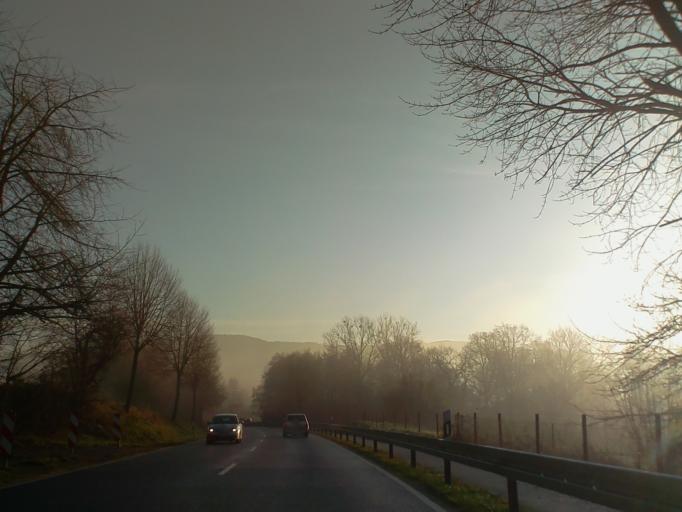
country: DE
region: Hesse
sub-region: Regierungsbezirk Darmstadt
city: Rimbach
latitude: 49.6414
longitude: 8.7590
